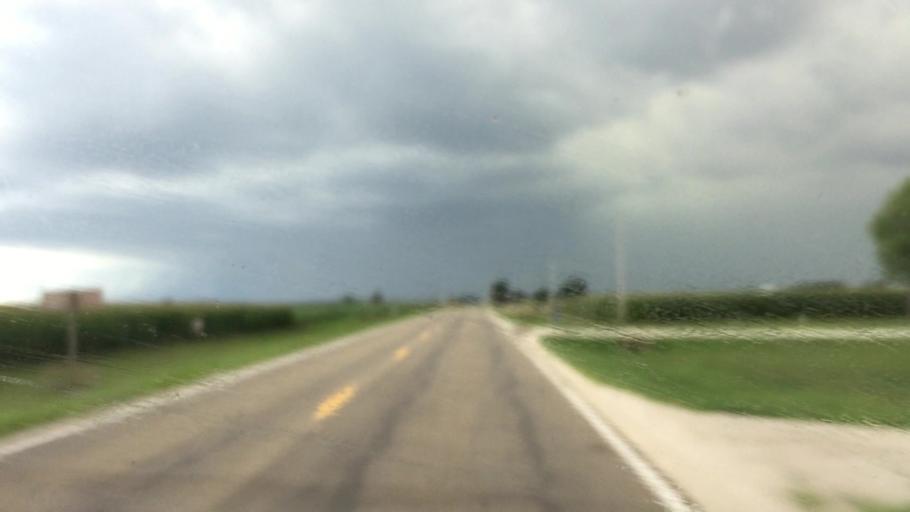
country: US
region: Iowa
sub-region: Henry County
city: Mount Pleasant
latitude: 40.7842
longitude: -91.5174
